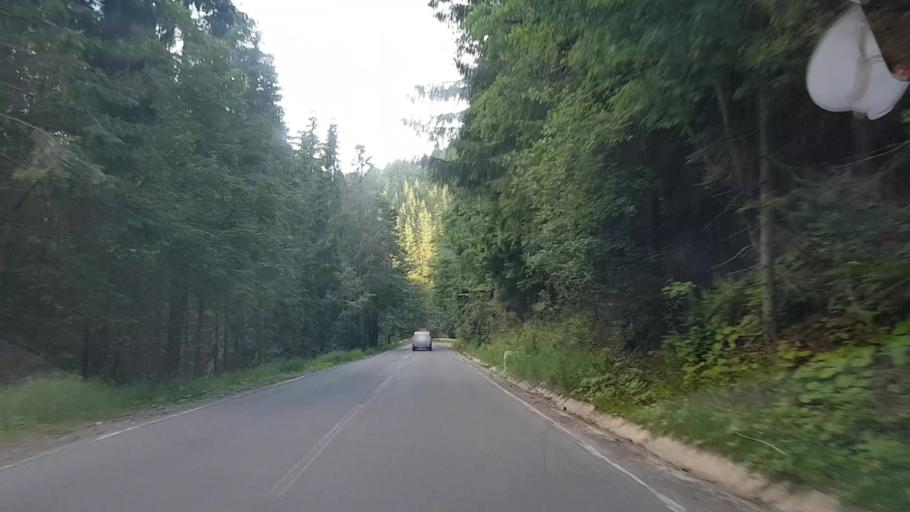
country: RO
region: Harghita
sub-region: Comuna Varsag
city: Varsag
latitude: 46.6362
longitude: 25.2658
